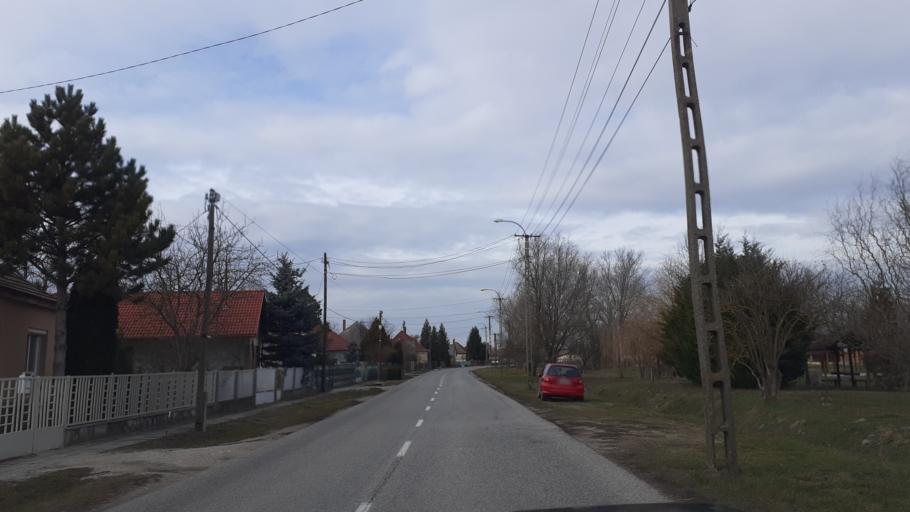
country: HU
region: Fejer
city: Szabadbattyan
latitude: 47.0762
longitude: 18.4140
